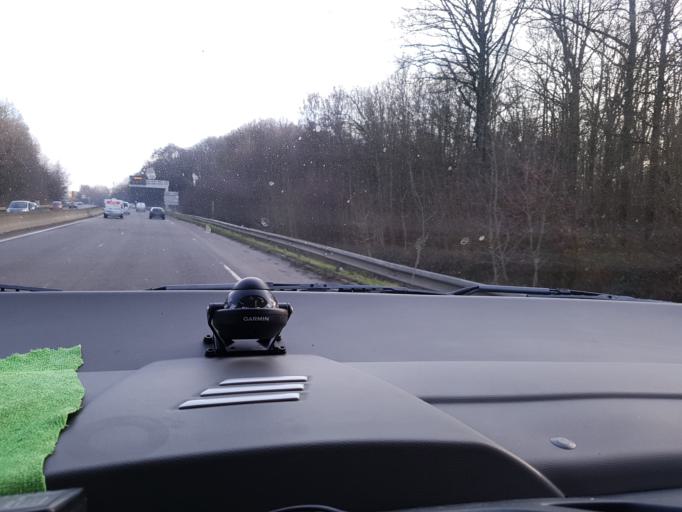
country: FR
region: Champagne-Ardenne
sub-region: Departement des Ardennes
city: Prix-les-Mezieres
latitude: 49.7462
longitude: 4.7043
